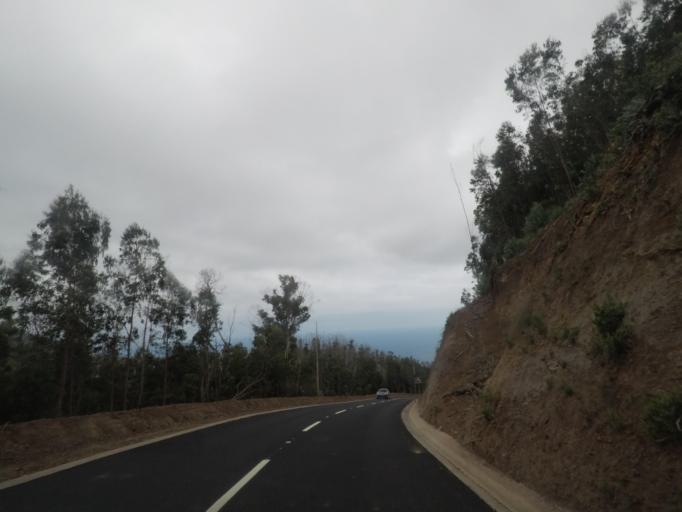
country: PT
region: Madeira
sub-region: Calheta
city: Estreito da Calheta
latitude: 32.7439
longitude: -17.1589
